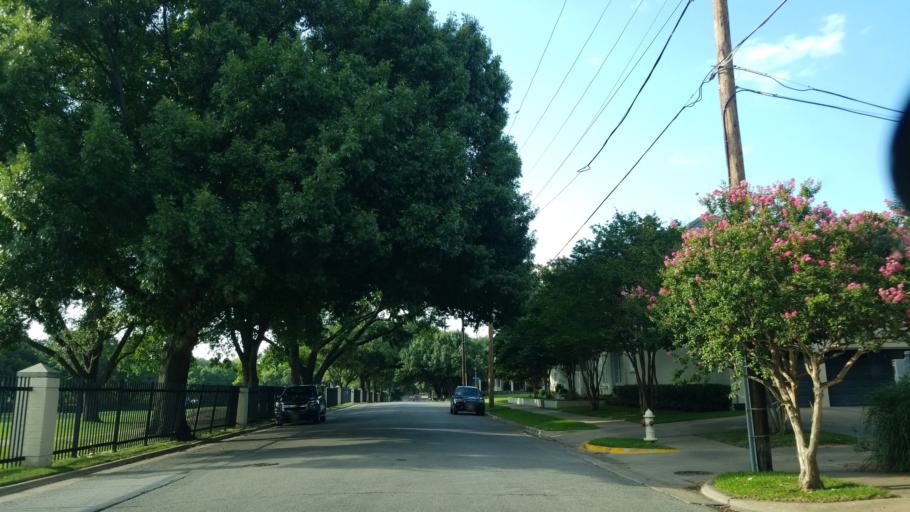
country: US
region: Texas
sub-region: Dallas County
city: Highland Park
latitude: 32.8344
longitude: -96.7988
